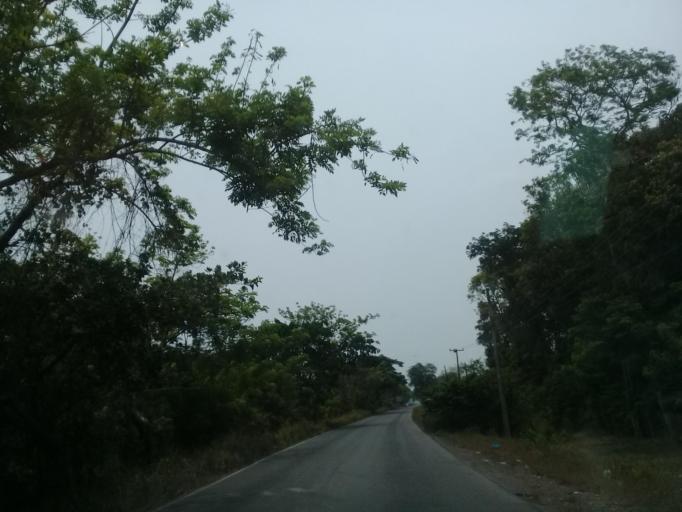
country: MX
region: Veracruz
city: El Tejar
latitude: 19.0460
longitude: -96.1935
